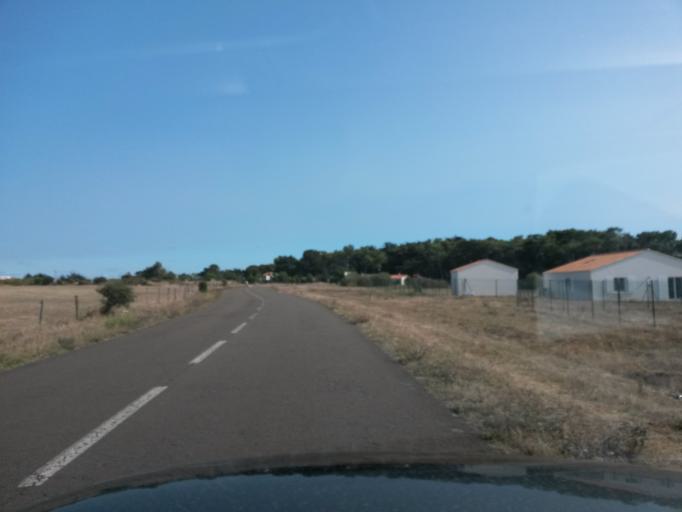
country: FR
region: Pays de la Loire
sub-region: Departement de la Vendee
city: Bretignolles-sur-Mer
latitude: 46.6127
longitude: -1.8516
